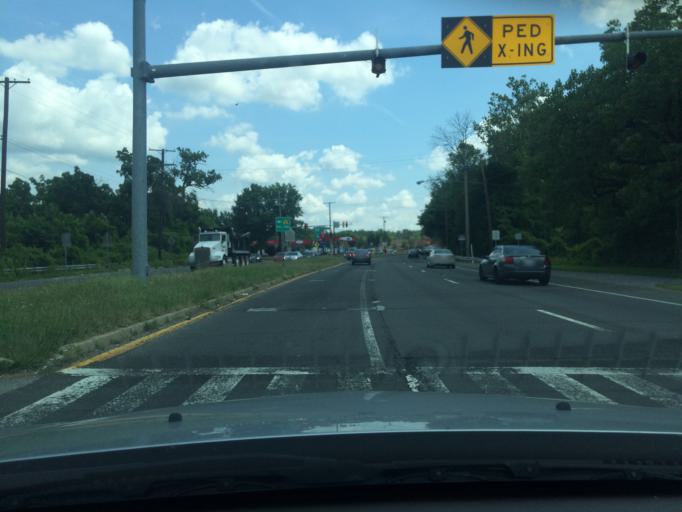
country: US
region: Maryland
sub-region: Prince George's County
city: Mount Rainier
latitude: 38.9531
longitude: -76.9660
